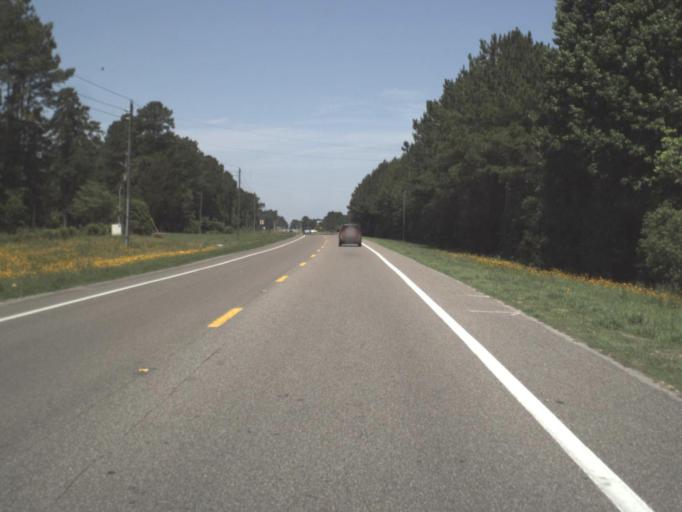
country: US
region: Florida
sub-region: Suwannee County
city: Live Oak
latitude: 30.2786
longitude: -82.9426
